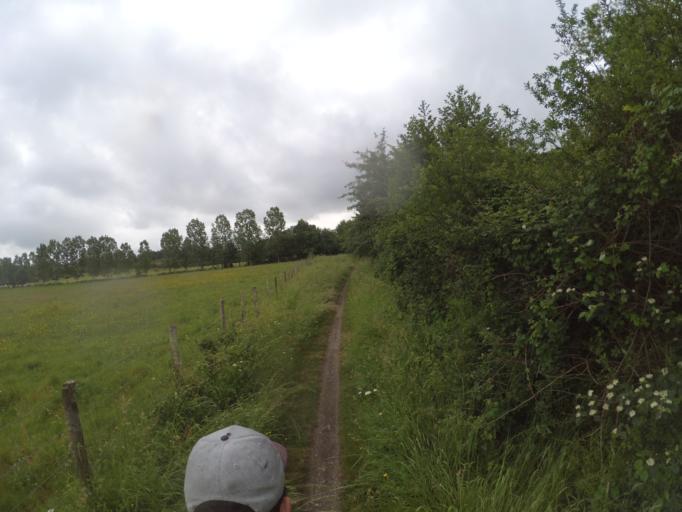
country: FR
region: Pays de la Loire
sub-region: Departement de la Vendee
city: Nesmy
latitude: 46.6163
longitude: -1.4042
